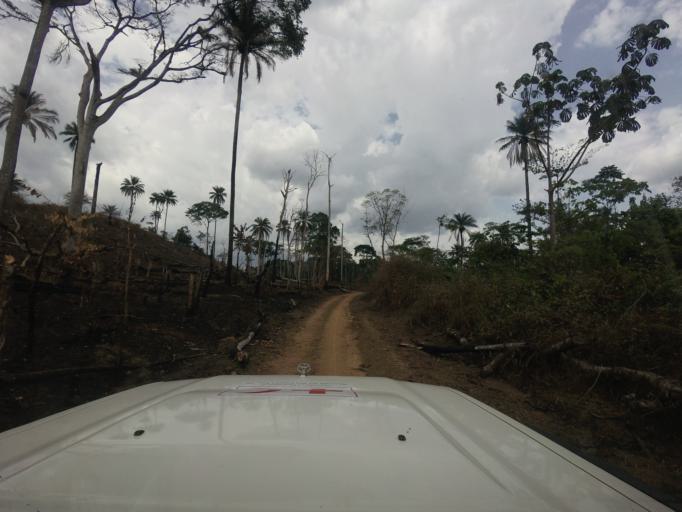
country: LR
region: Lofa
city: Voinjama
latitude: 8.3928
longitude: -9.6043
